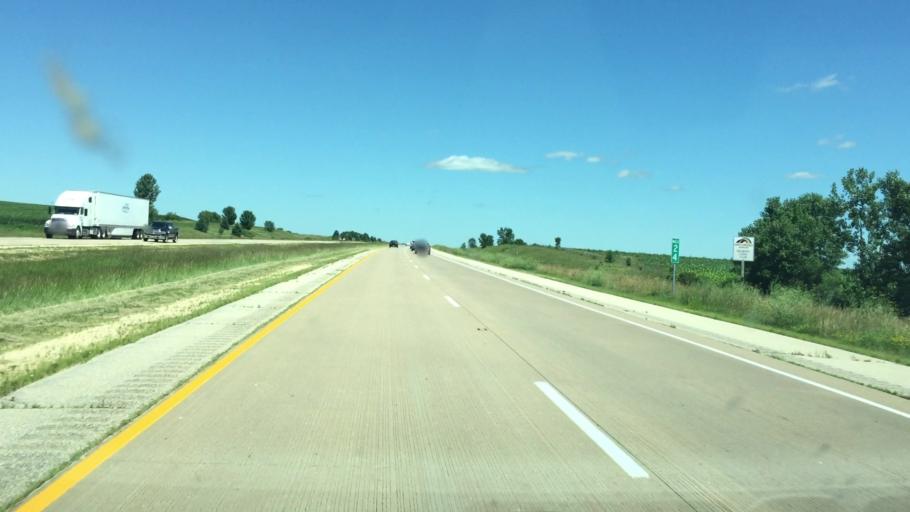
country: US
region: Wisconsin
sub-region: Grant County
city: Platteville
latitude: 42.7400
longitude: -90.3812
